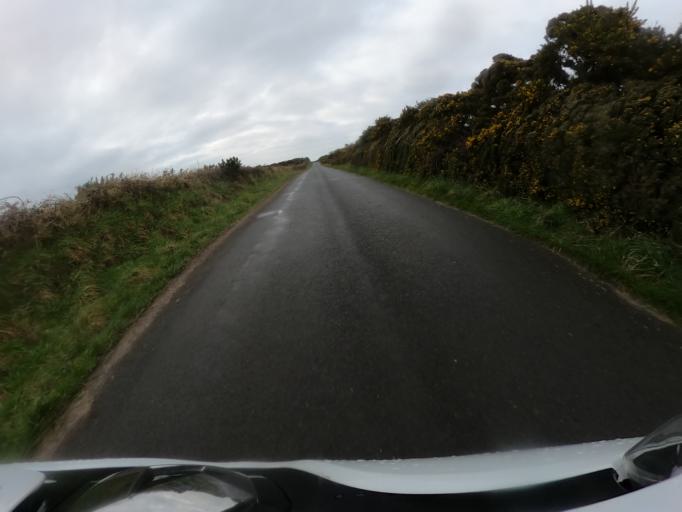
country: IM
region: Ramsey
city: Ramsey
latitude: 54.3490
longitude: -4.5233
